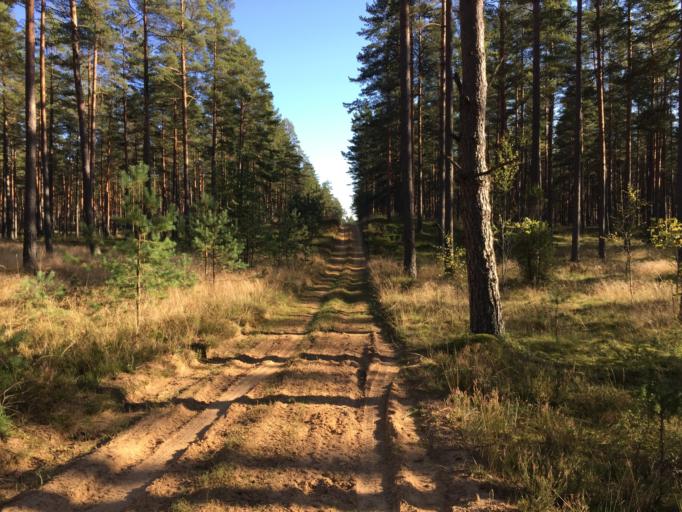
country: LV
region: Garkalne
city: Garkalne
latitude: 57.0213
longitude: 24.3650
